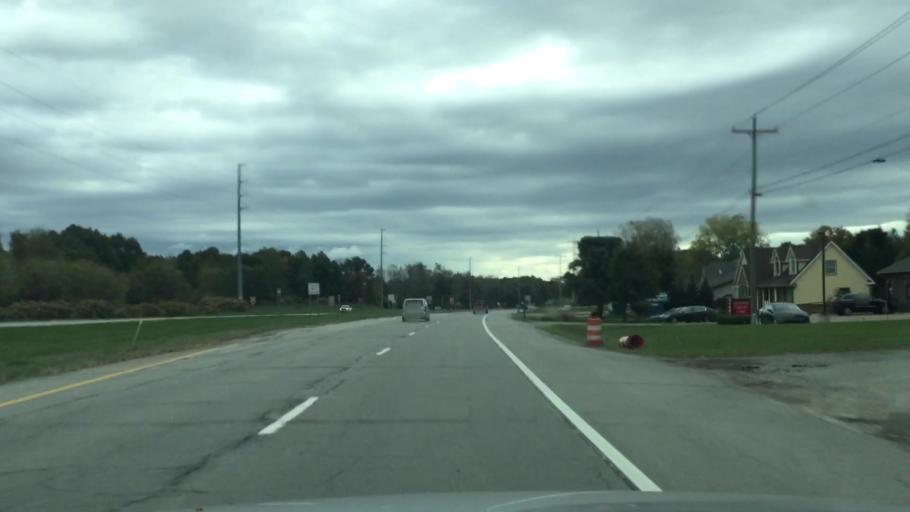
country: US
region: Michigan
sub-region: Livingston County
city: Brighton
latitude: 42.6360
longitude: -83.7280
